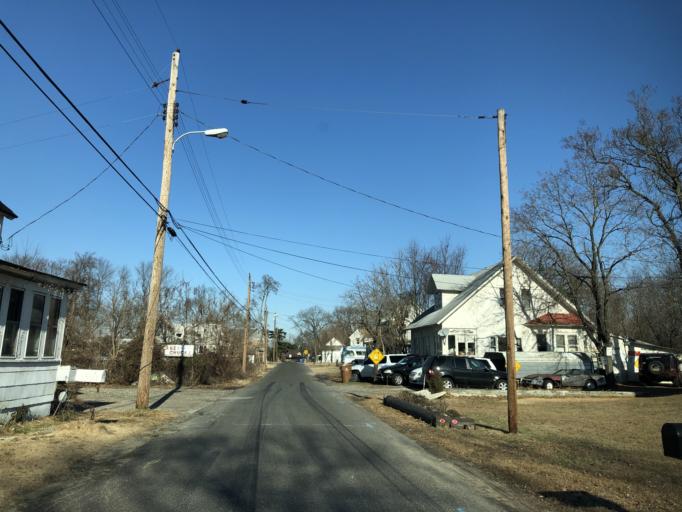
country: US
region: New Jersey
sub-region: Gloucester County
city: Beckett
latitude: 39.7956
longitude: -75.3534
